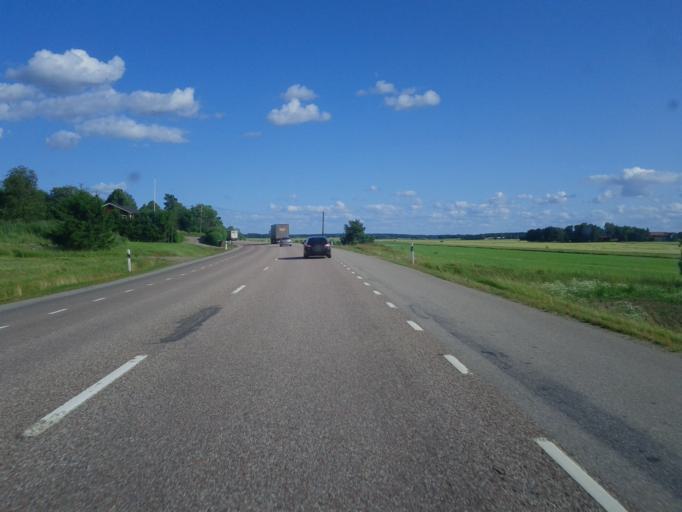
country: SE
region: Uppsala
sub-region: Enkopings Kommun
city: Irsta
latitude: 59.7060
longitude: 16.9867
